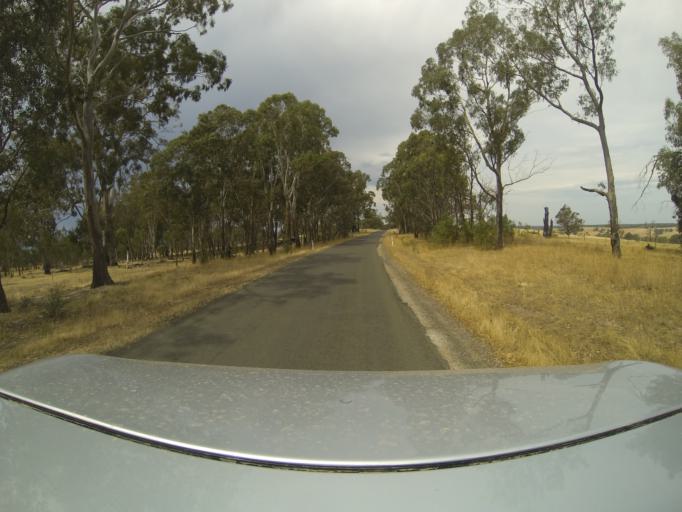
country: AU
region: Victoria
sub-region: Wellington
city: Heyfield
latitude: -37.9074
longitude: 146.7091
